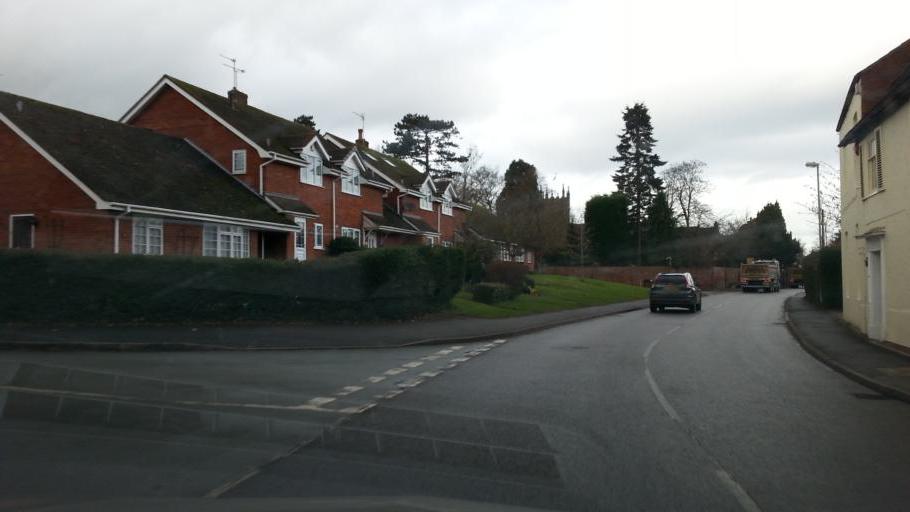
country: GB
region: England
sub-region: Staffordshire
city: Alrewas
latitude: 52.7672
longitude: -1.7910
